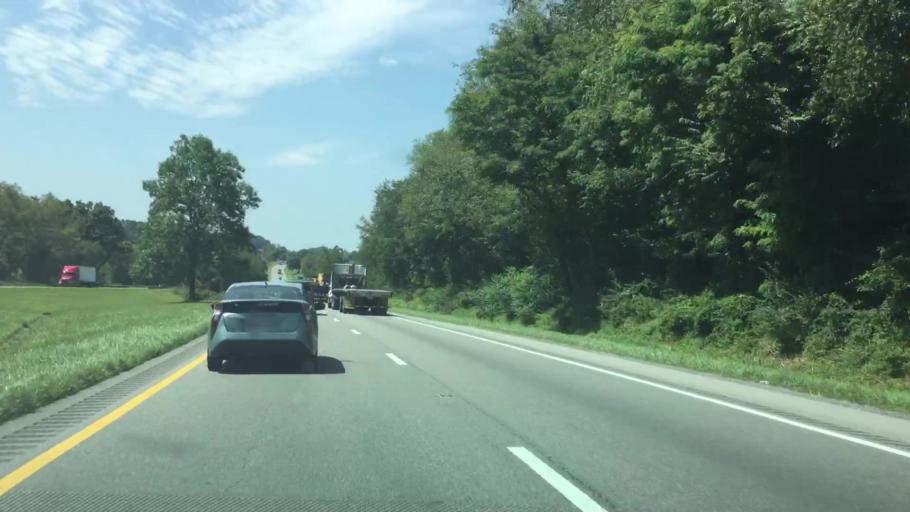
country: US
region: Virginia
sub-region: Washington County
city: Emory
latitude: 36.7489
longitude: -81.8832
